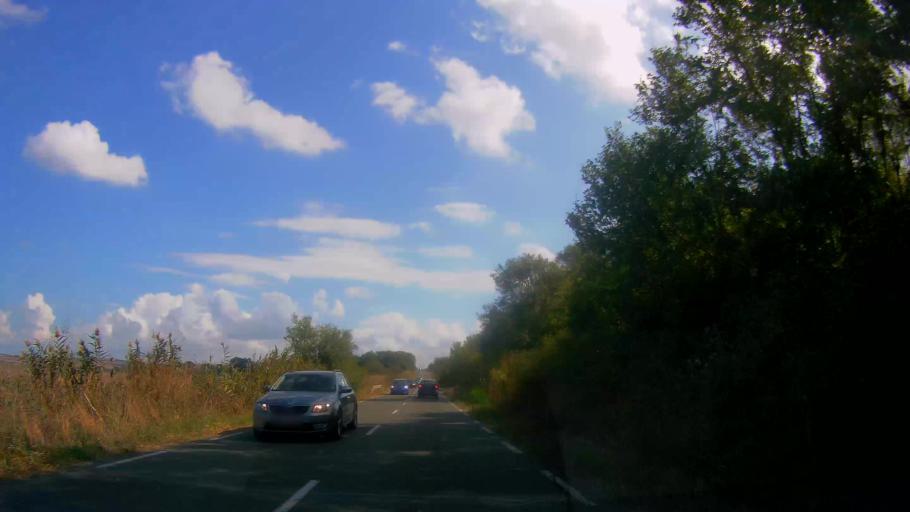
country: BG
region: Burgas
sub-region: Obshtina Kameno
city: Kameno
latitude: 42.4856
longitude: 27.3419
